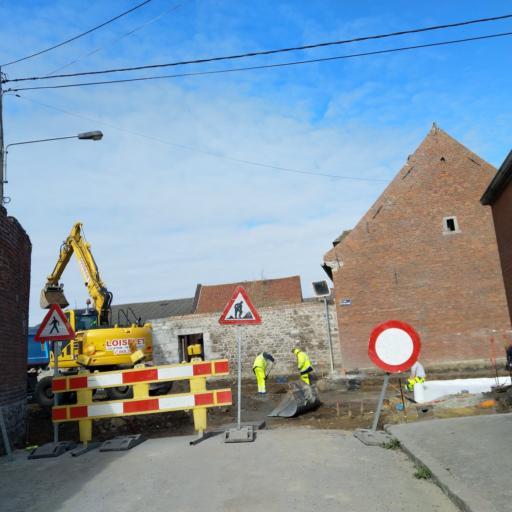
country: BE
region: Wallonia
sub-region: Province du Hainaut
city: Brugelette
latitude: 50.5882
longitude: 3.8770
